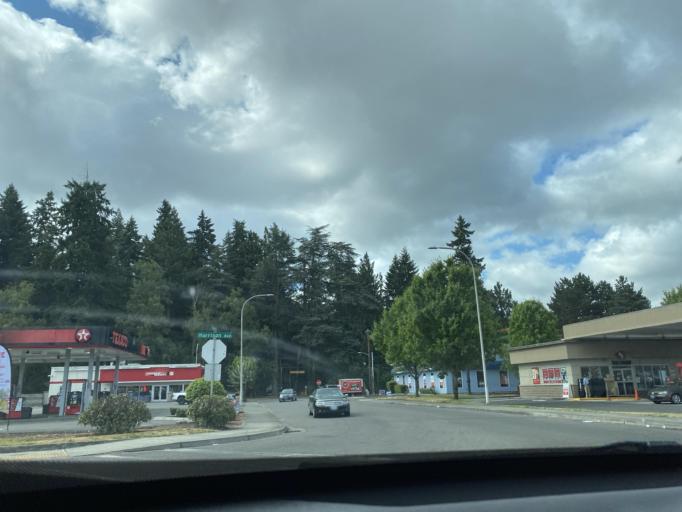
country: US
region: Washington
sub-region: Lewis County
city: Fords Prairie
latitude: 46.7281
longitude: -122.9793
